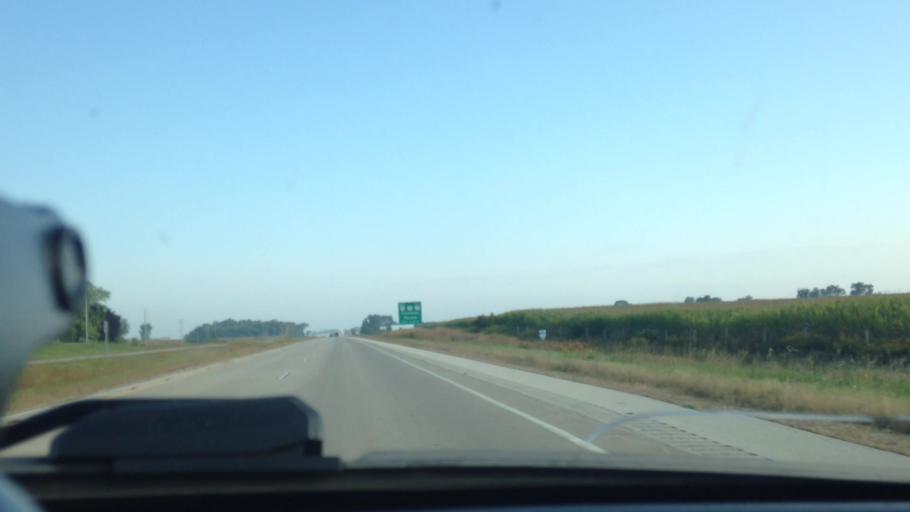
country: US
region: Wisconsin
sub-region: Oconto County
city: Oconto Falls
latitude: 45.0388
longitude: -88.0444
